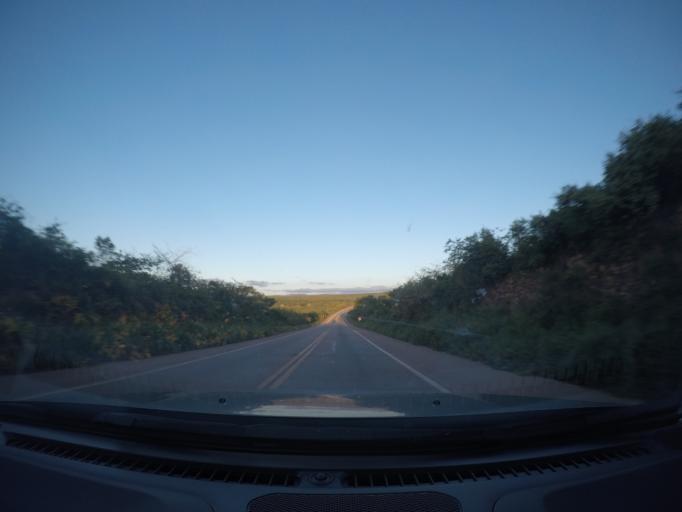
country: BR
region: Bahia
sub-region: Seabra
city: Seabra
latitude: -12.3946
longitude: -41.9288
